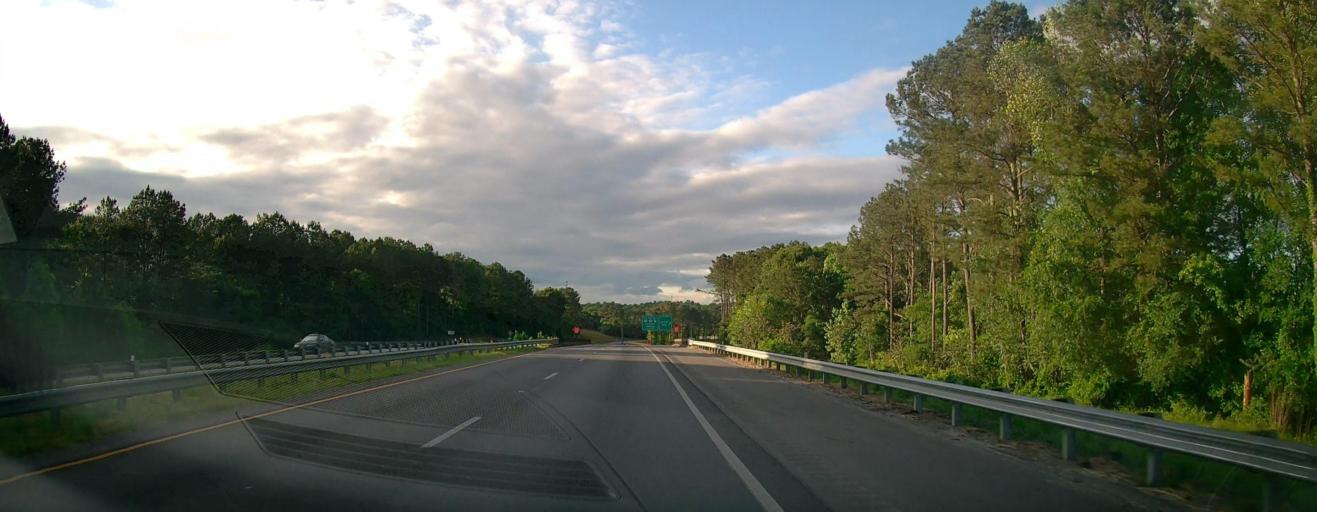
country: US
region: Georgia
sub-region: Clarke County
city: Athens
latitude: 33.9706
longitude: -83.3545
